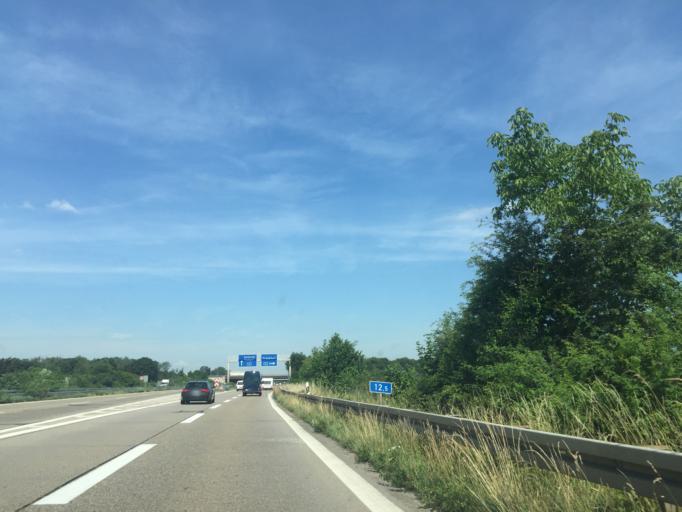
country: DE
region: Baden-Wuerttemberg
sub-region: Karlsruhe Region
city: Eppelheim
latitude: 49.4154
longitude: 8.6398
